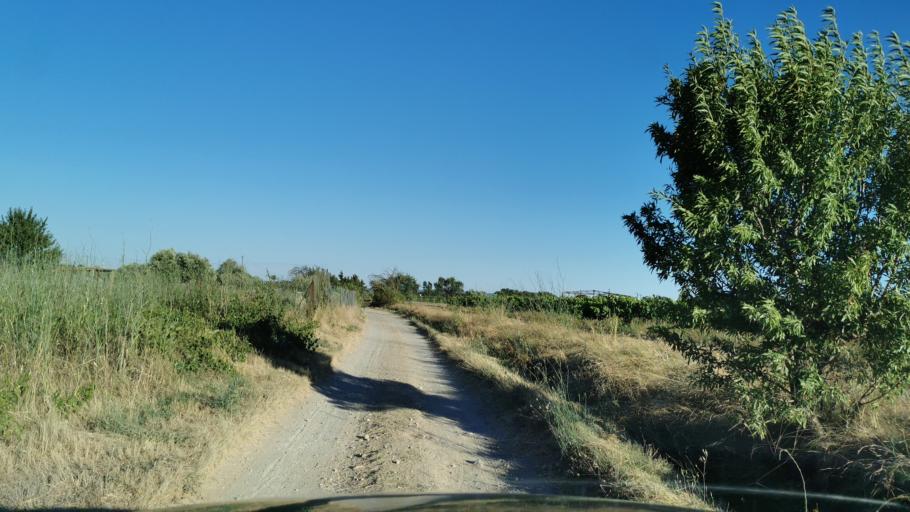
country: FR
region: Languedoc-Roussillon
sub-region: Departement de l'Aude
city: Ouveillan
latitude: 43.2652
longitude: 2.9831
